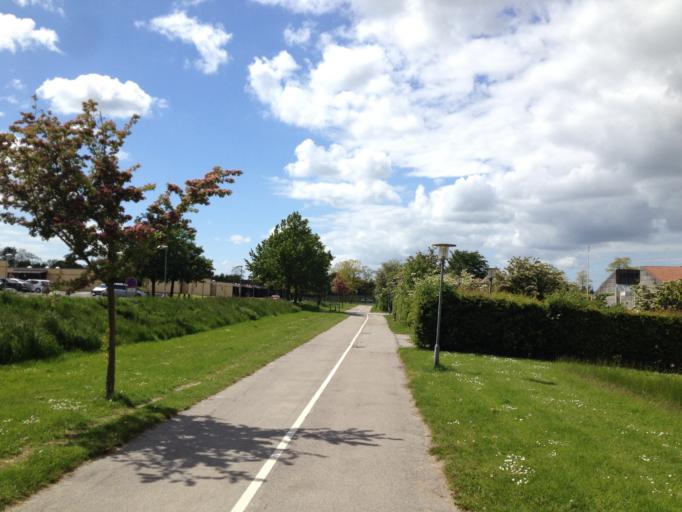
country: DK
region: Capital Region
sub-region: Fredensborg Kommune
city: Niva
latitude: 55.9397
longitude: 12.4913
